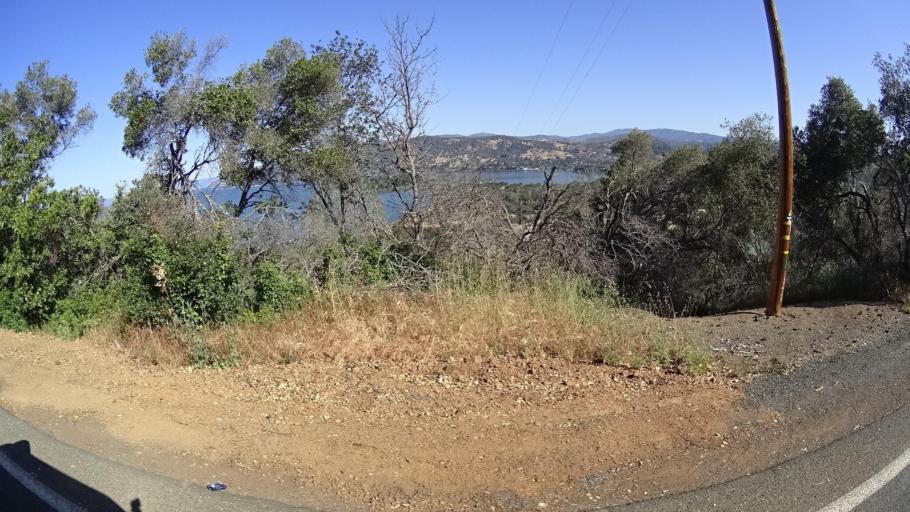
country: US
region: California
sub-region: Lake County
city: Clearlake Oaks
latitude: 38.9981
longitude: -122.6652
